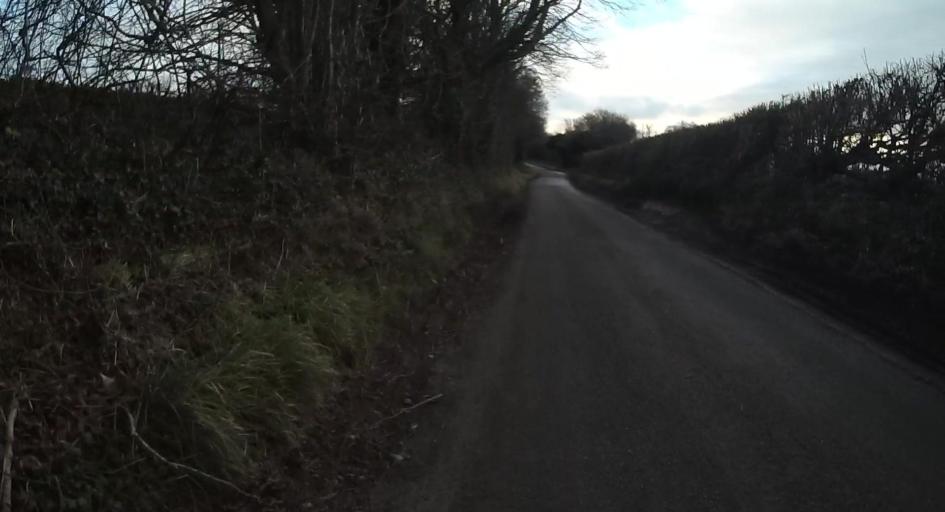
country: GB
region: England
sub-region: Hampshire
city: Swanmore
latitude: 51.0382
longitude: -1.1615
